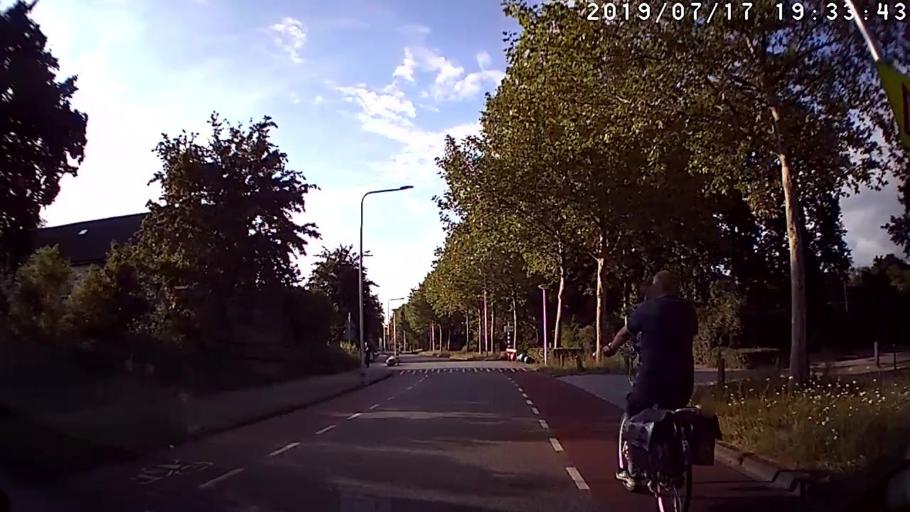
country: NL
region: Overijssel
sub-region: Gemeente Zwolle
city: Zwolle
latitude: 52.5345
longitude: 6.0995
